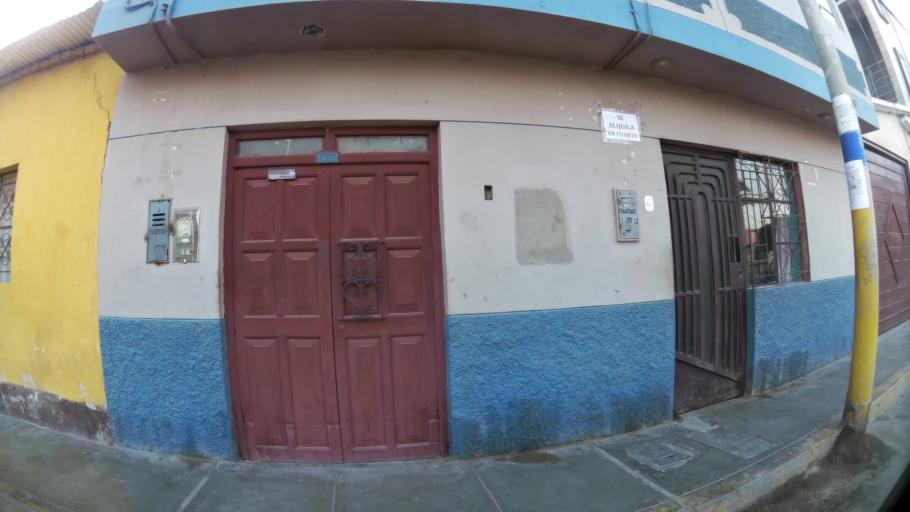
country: PE
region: Lambayeque
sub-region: Provincia de Chiclayo
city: Santa Rosa
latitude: -6.7651
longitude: -79.8336
